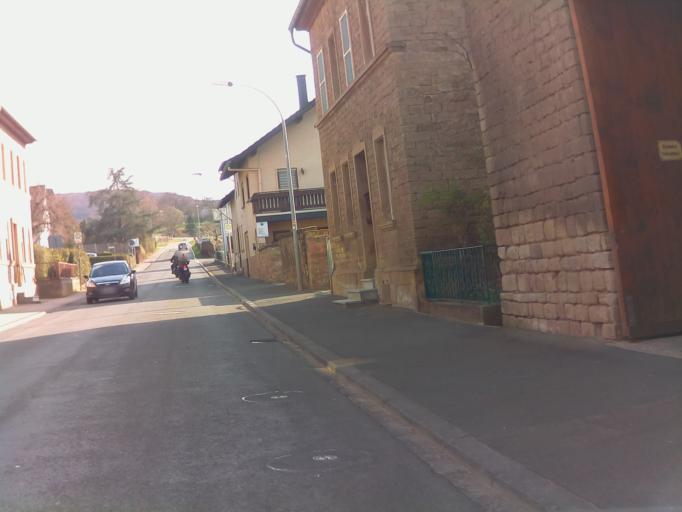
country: DE
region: Rheinland-Pfalz
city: Meddersheim
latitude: 49.7762
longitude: 7.6152
